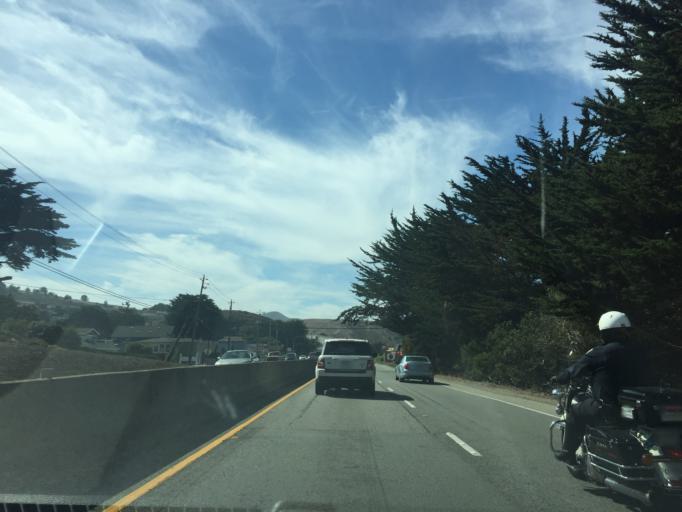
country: US
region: California
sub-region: San Mateo County
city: Pacifica
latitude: 37.6104
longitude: -122.4927
